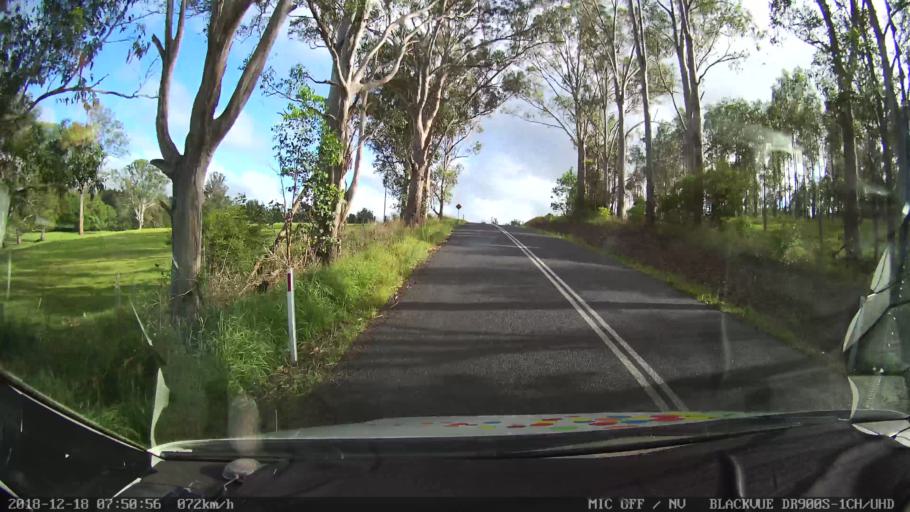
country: AU
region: New South Wales
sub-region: Kyogle
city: Kyogle
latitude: -28.4408
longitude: 152.5744
